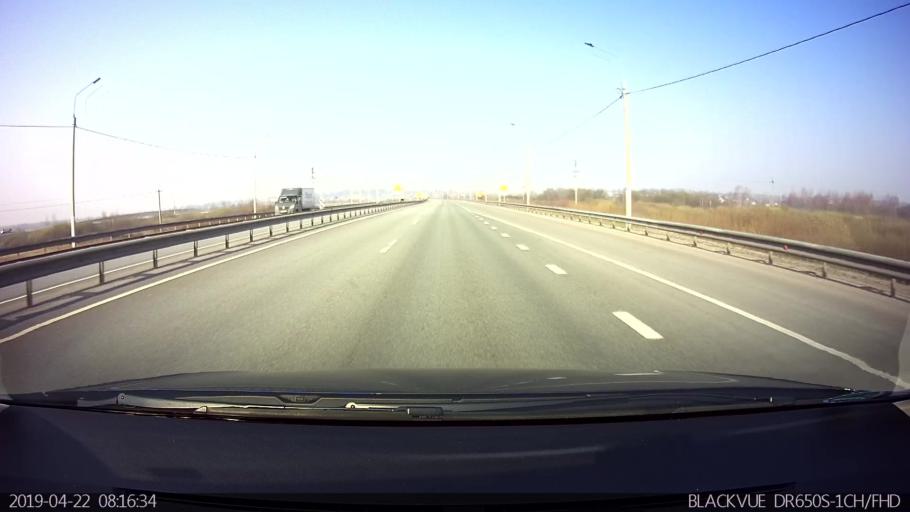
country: RU
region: Smolensk
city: Yartsevo
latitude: 55.0792
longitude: 32.6899
